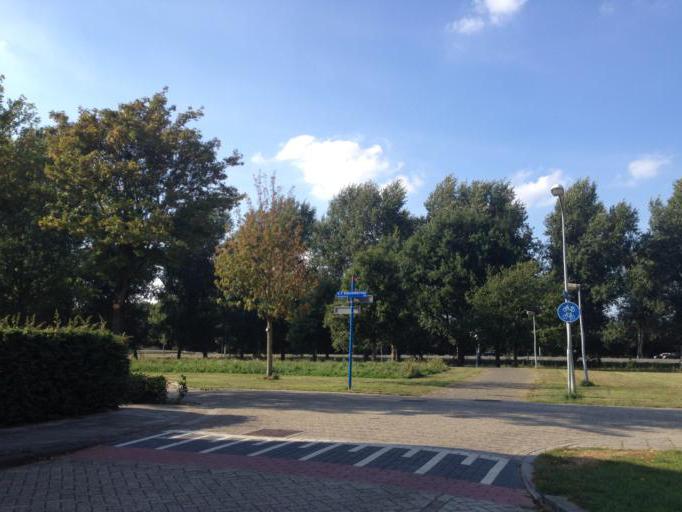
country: NL
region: Flevoland
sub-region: Gemeente Almere
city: Almere Stad
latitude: 52.4006
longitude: 5.2582
